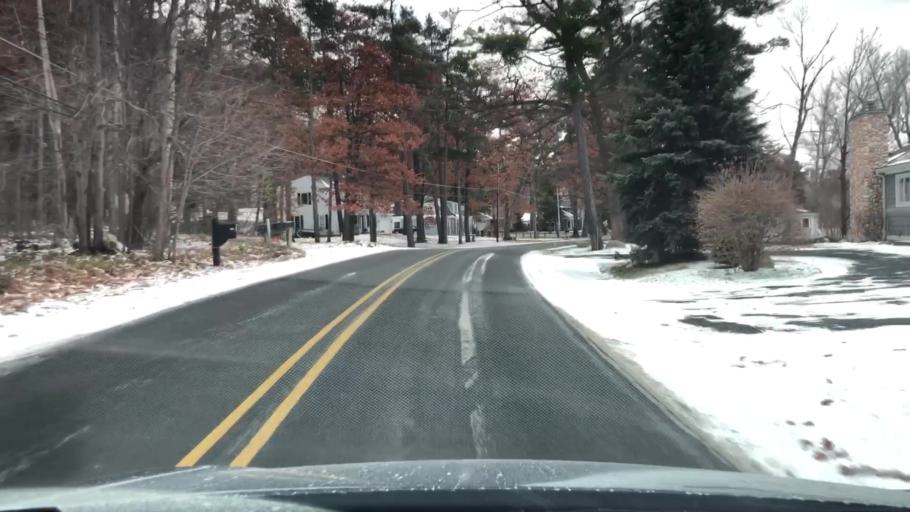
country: US
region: Michigan
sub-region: Grand Traverse County
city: Traverse City
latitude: 44.8155
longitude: -85.5783
